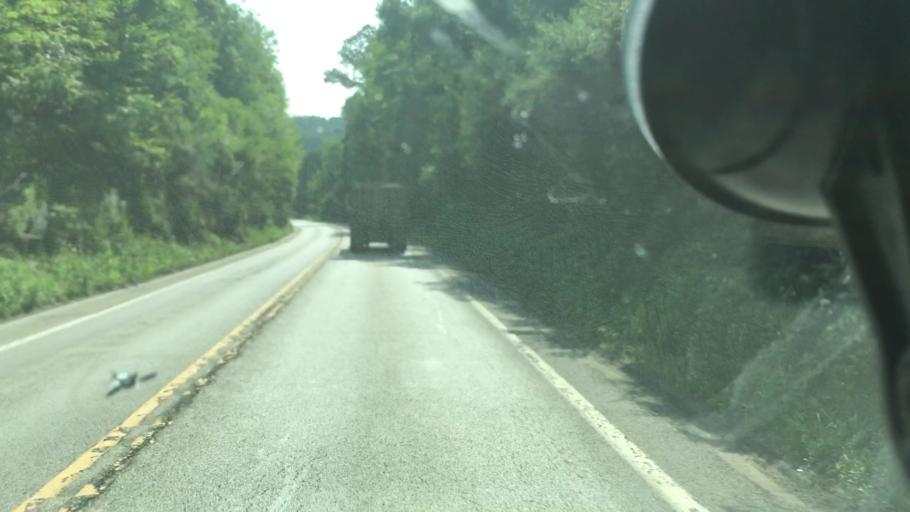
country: US
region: Pennsylvania
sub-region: Butler County
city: Slippery Rock
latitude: 41.0231
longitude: -80.1938
